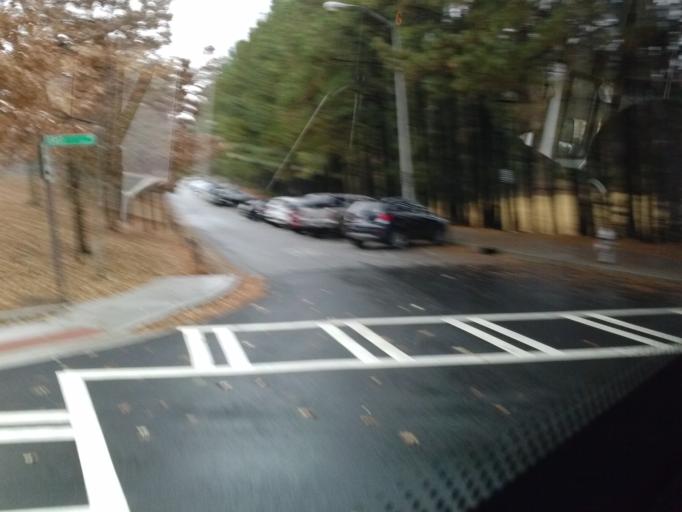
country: US
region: Georgia
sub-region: Fulton County
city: Atlanta
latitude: 33.7772
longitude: -84.4024
